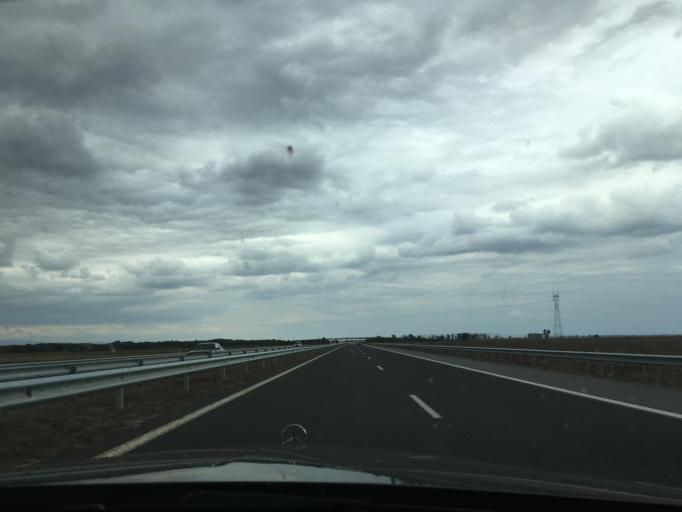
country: BG
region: Stara Zagora
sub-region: Obshtina Radnevo
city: Radnevo
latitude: 42.3719
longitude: 25.8082
